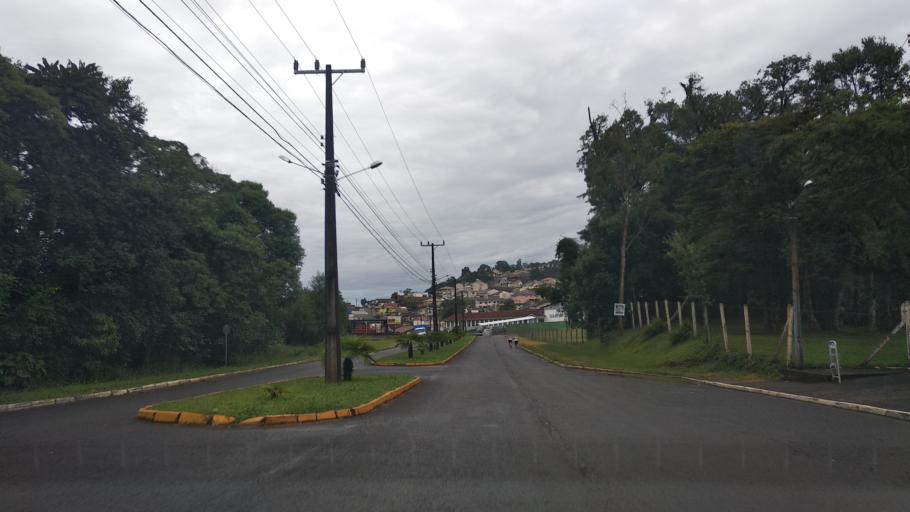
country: BR
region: Santa Catarina
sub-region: Videira
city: Videira
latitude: -26.9893
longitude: -51.1810
